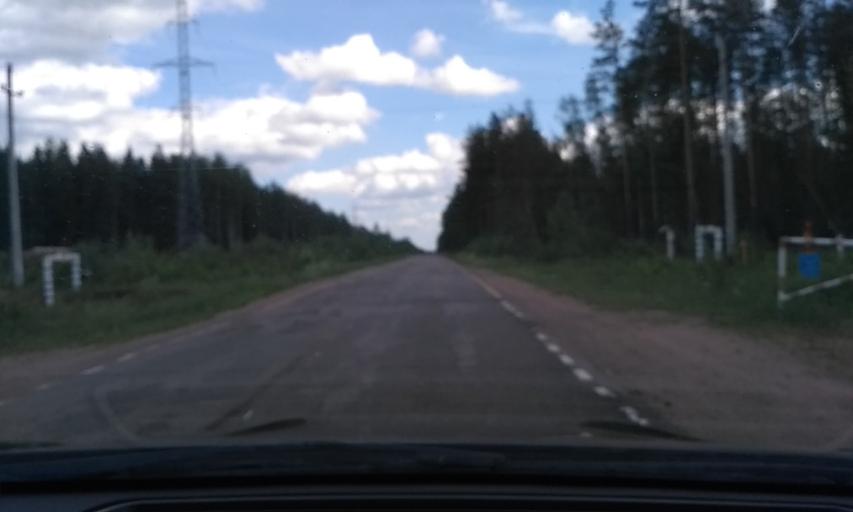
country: RU
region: Leningrad
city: Otradnoye
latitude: 59.8217
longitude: 30.7700
